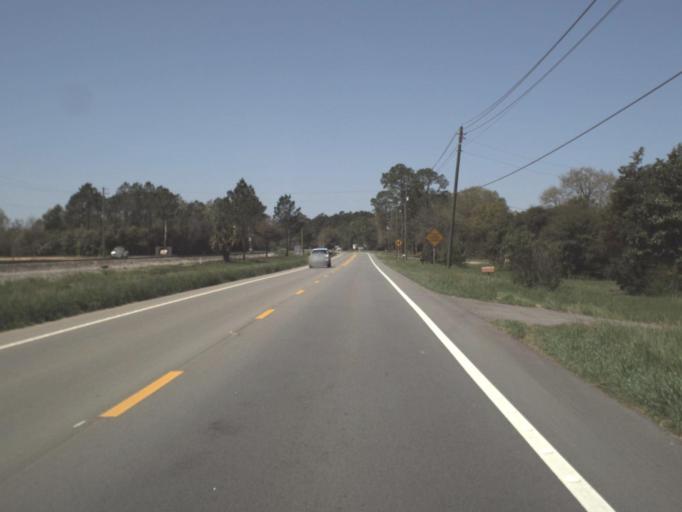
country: US
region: Florida
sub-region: Walton County
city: DeFuniak Springs
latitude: 30.7276
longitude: -86.0755
